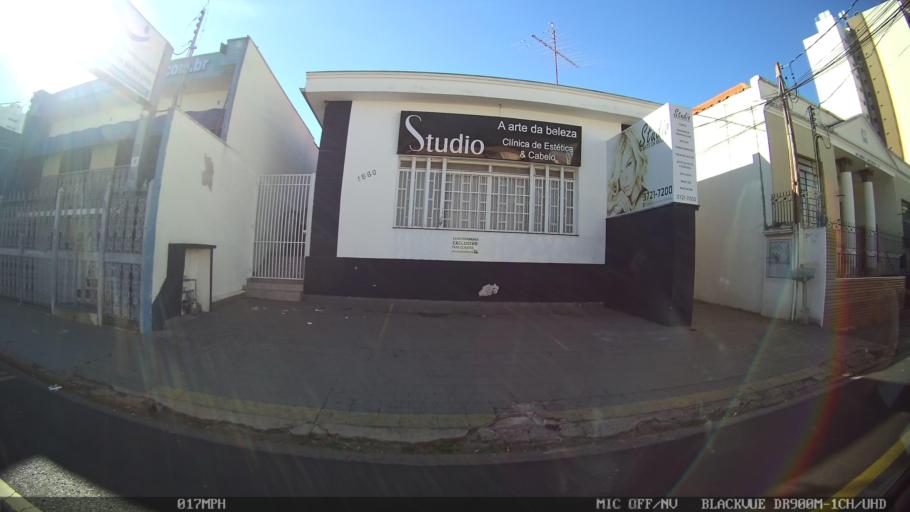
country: BR
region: Sao Paulo
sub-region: Franca
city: Franca
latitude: -20.5398
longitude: -47.4036
